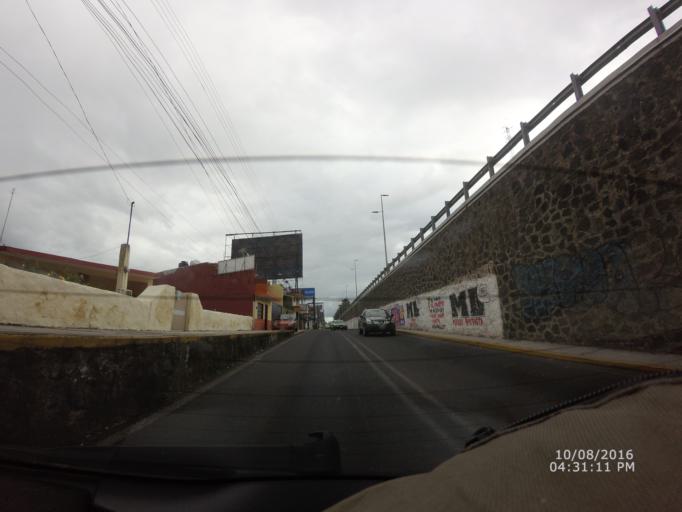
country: MX
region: Veracruz
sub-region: Xalapa
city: Xalapa de Enriquez
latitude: 19.5505
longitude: -96.9125
